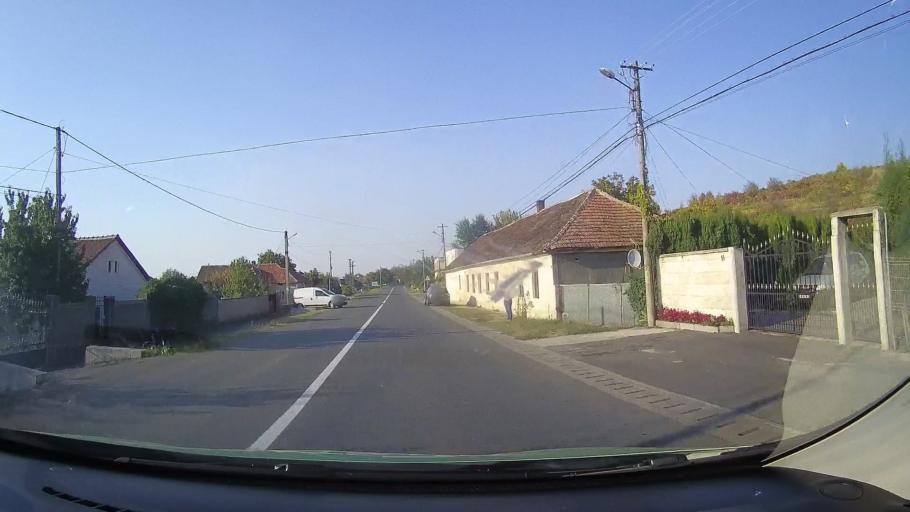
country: RO
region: Arad
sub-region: Comuna Ghioroc
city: Cuvin
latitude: 46.1599
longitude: 21.5926
